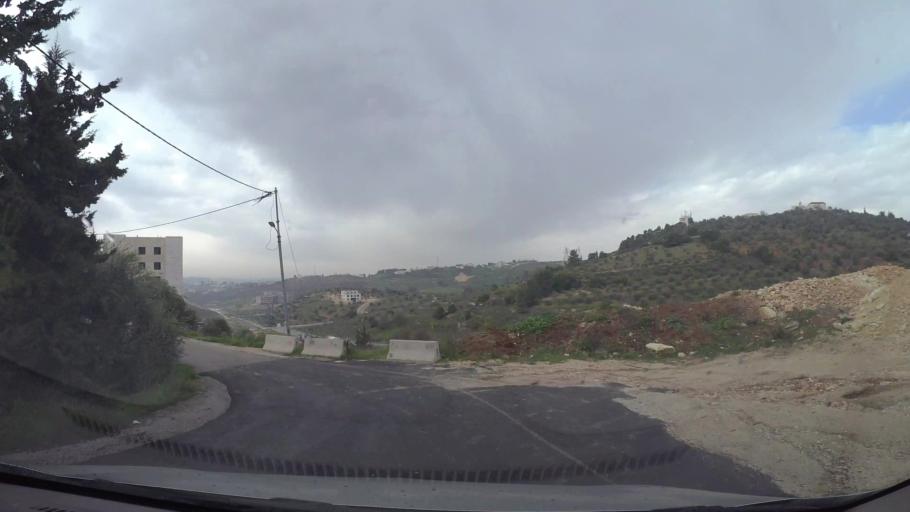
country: JO
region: Amman
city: Wadi as Sir
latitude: 31.9889
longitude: 35.8152
